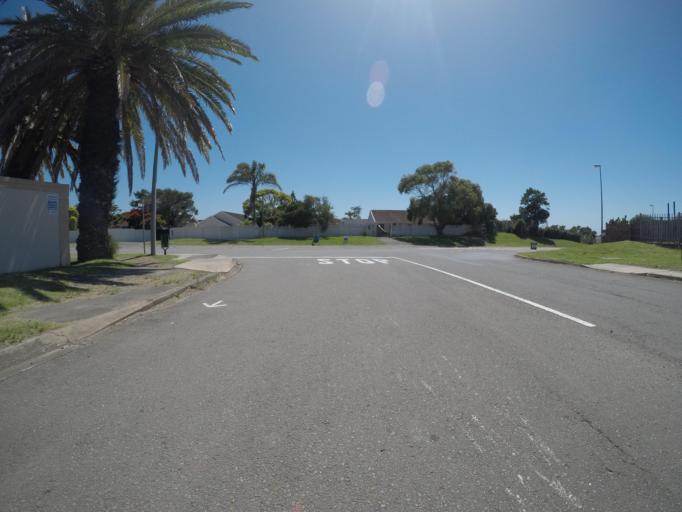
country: ZA
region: Eastern Cape
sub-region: Buffalo City Metropolitan Municipality
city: East London
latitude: -32.9705
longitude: 27.9508
